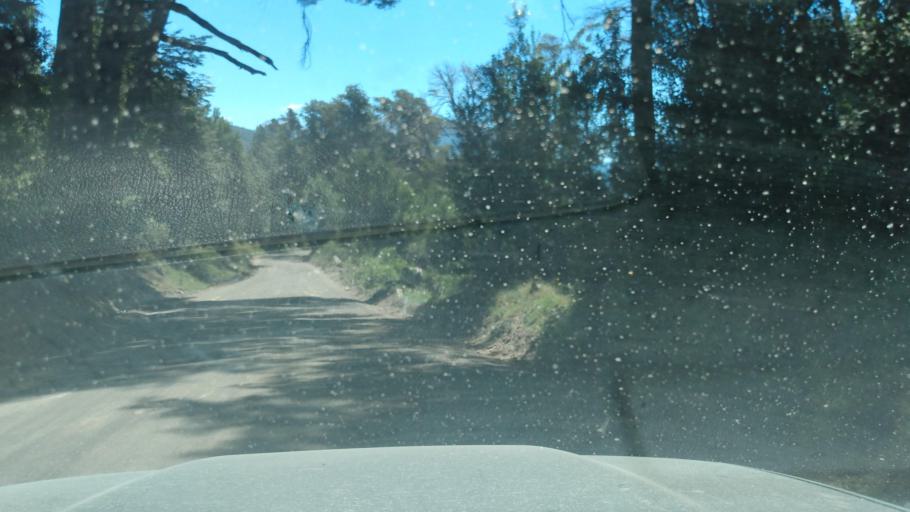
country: AR
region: Neuquen
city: Villa La Angostura
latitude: -40.6481
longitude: -71.4357
